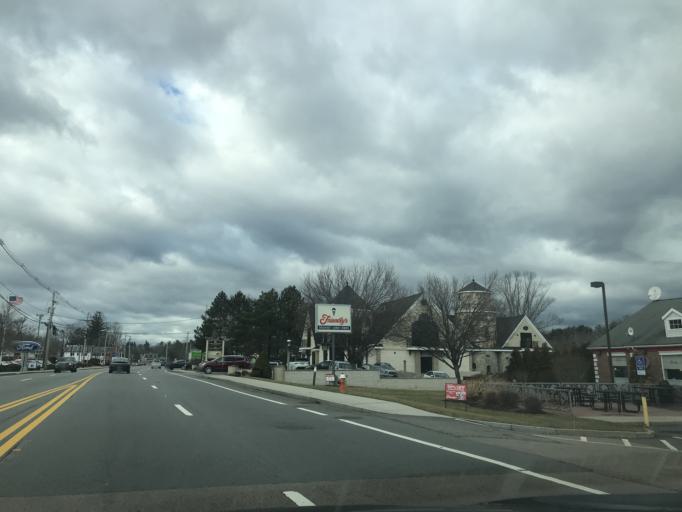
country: US
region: Massachusetts
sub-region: Plymouth County
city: Hanover
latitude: 42.1534
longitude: -70.8465
